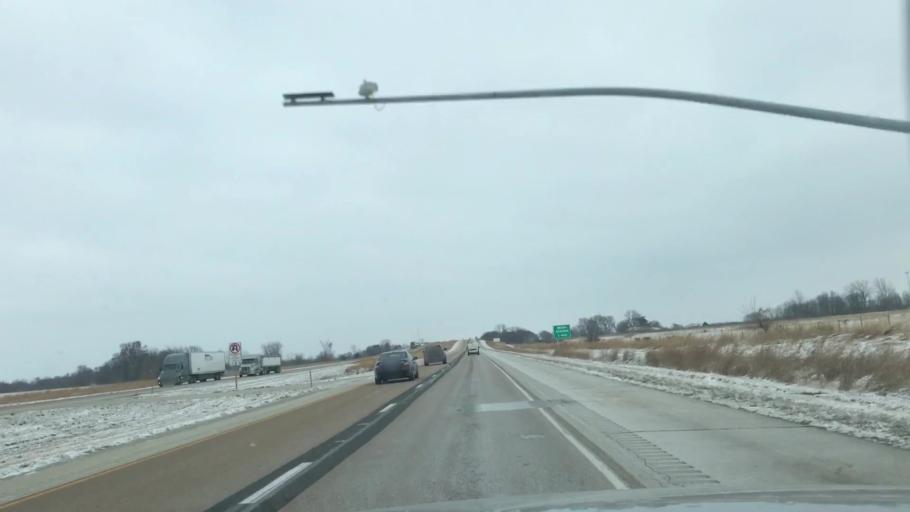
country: US
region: Illinois
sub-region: Montgomery County
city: Litchfield
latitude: 39.2087
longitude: -89.6563
